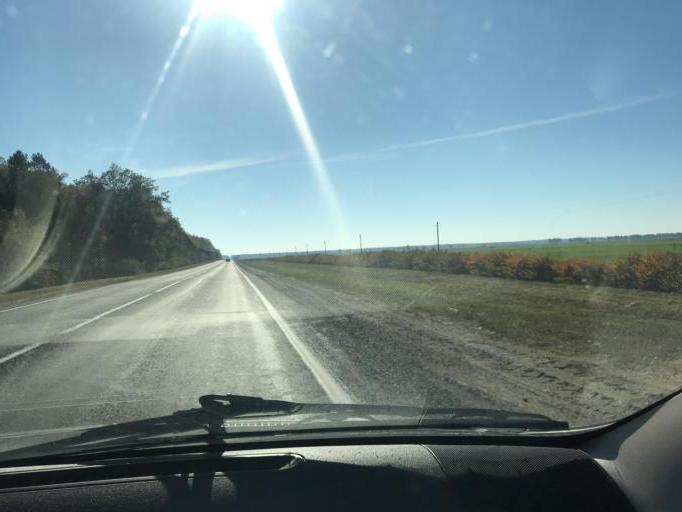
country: BY
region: Minsk
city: Starobin
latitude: 52.5399
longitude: 27.4734
